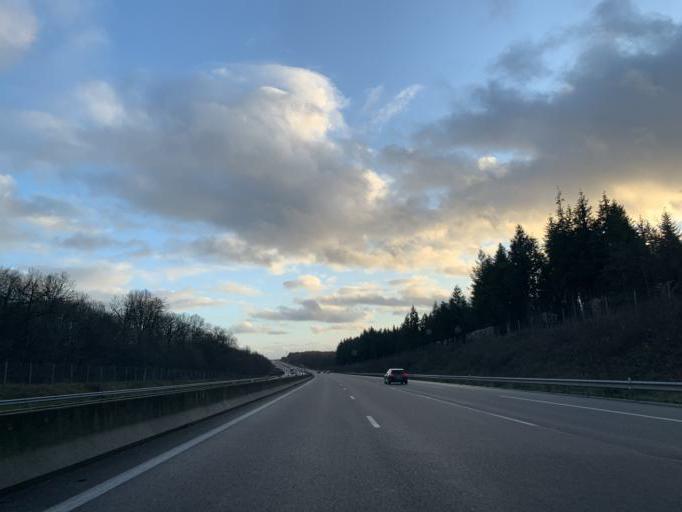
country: FR
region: Bourgogne
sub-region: Departement de la Cote-d'Or
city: Selongey
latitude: 47.6626
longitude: 5.1746
